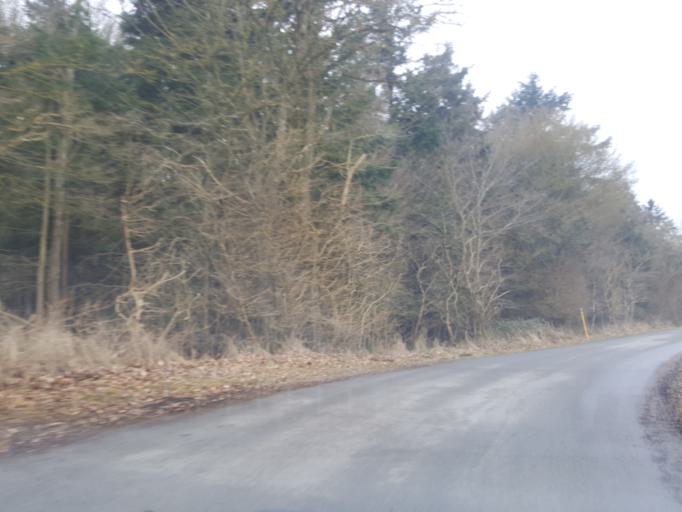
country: DK
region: Zealand
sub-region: Vordingborg Kommune
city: Neder Vindinge
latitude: 55.0390
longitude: 11.8146
